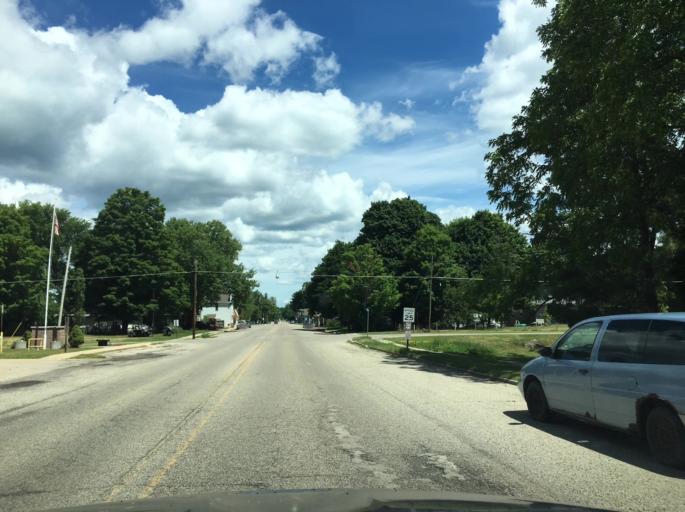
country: US
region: Michigan
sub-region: Osceola County
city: Reed City
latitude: 43.8481
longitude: -85.4444
